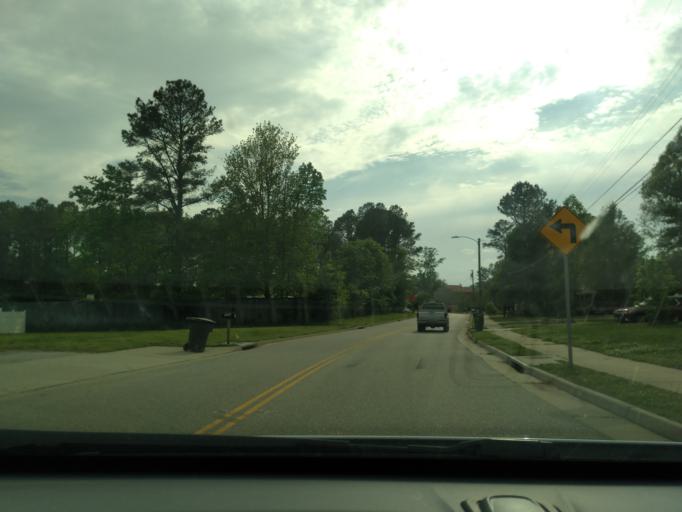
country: US
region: Virginia
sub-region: York County
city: Yorktown
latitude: 37.1679
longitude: -76.5201
